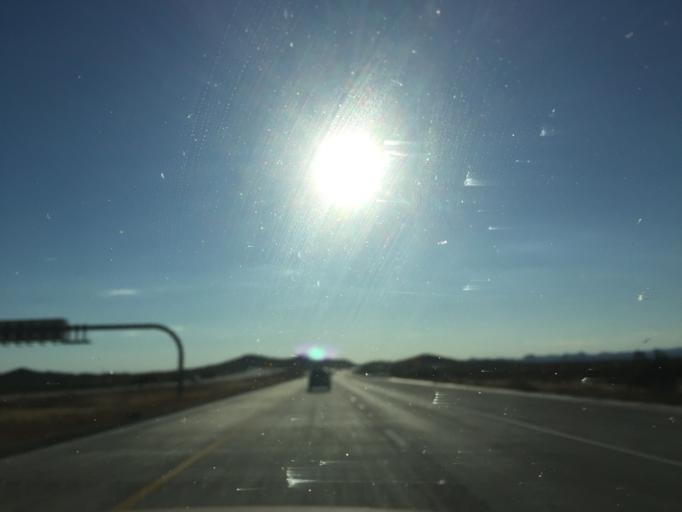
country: US
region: Arizona
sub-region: Maricopa County
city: Anthem
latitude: 33.7693
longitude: -112.1595
